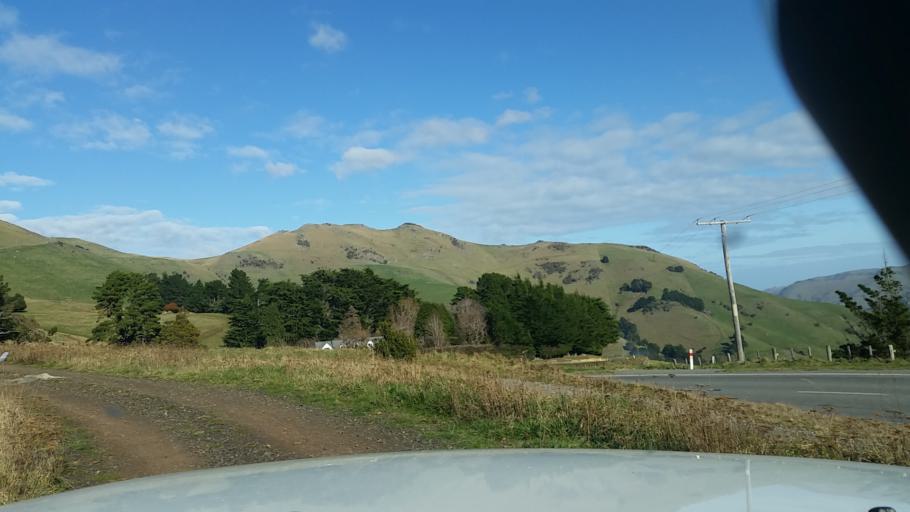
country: NZ
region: Canterbury
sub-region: Christchurch City
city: Christchurch
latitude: -43.7484
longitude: 172.8658
